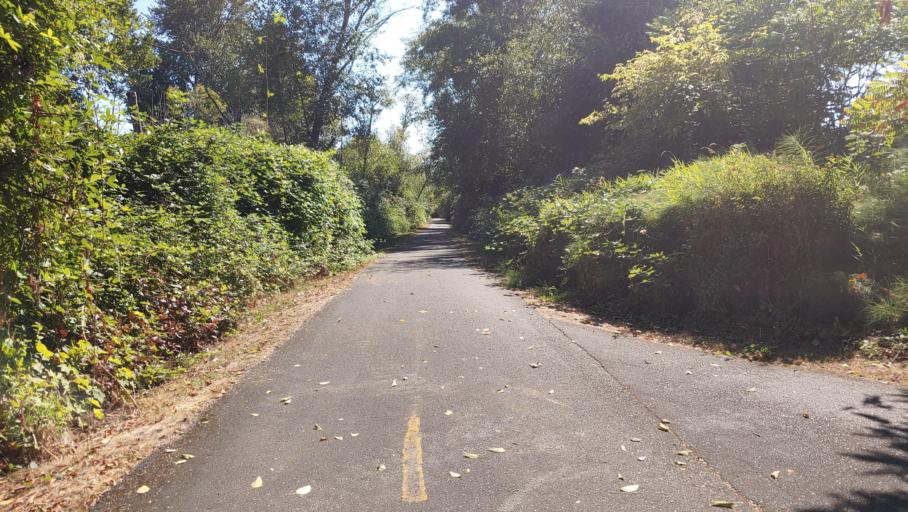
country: US
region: Washington
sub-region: King County
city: Renton
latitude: 47.4720
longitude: -122.2362
